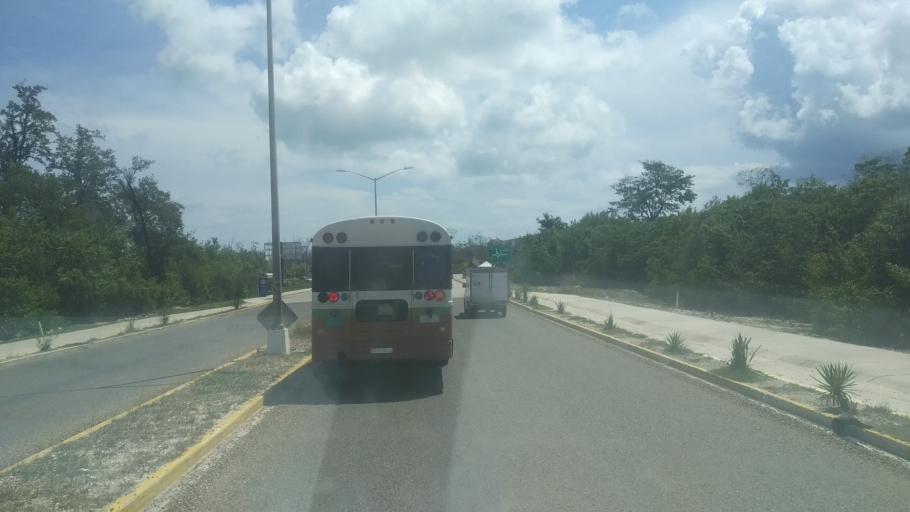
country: BZ
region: Belize
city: Belize City
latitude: 17.5016
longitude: -88.2222
